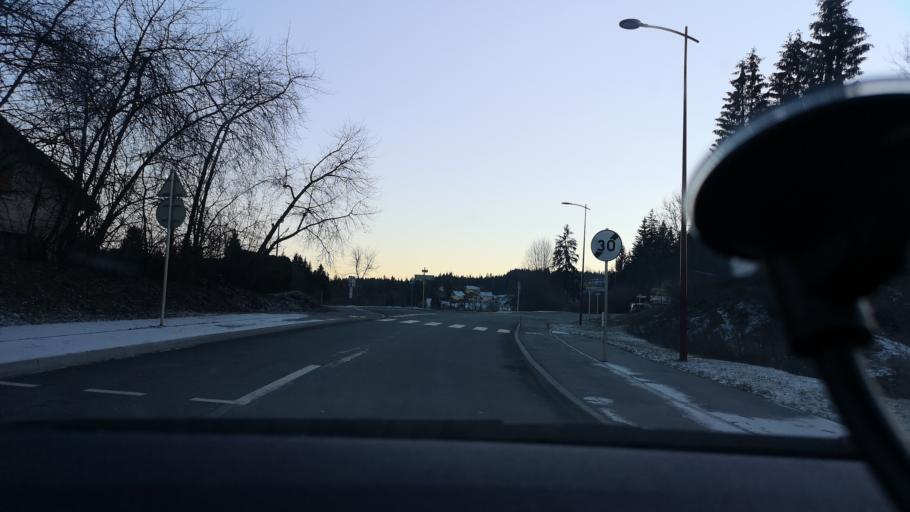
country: FR
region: Franche-Comte
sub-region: Departement du Doubs
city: Pontarlier
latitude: 46.8541
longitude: 6.3360
